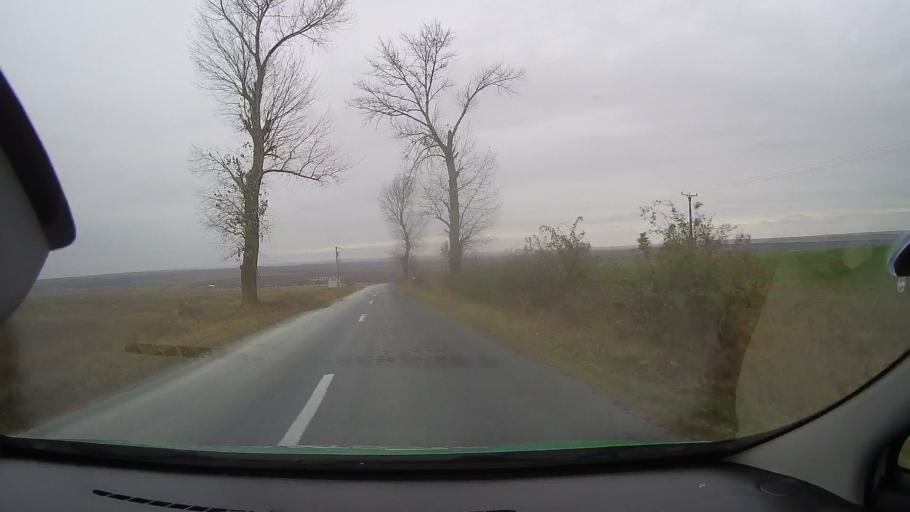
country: RO
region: Constanta
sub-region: Comuna Pantelimon
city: Pantelimon
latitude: 44.5872
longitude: 28.3155
